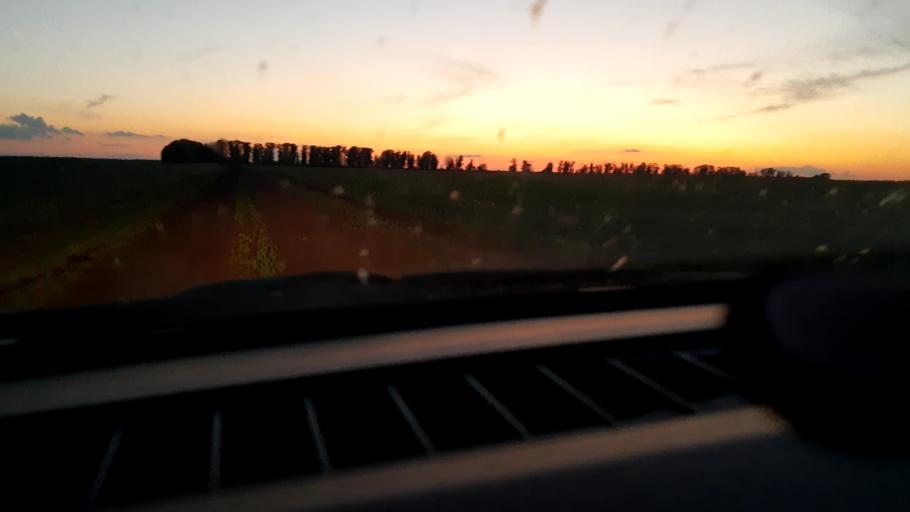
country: RU
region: Bashkortostan
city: Asanovo
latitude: 54.8621
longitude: 55.5855
